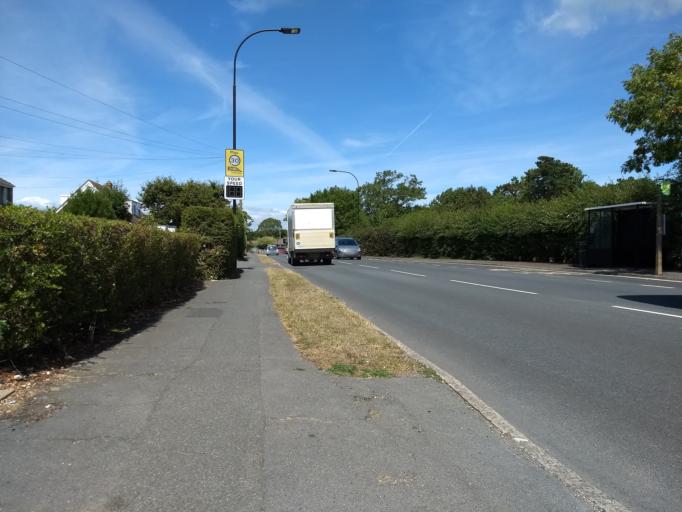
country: GB
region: England
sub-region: Isle of Wight
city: Northwood
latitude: 50.7417
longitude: -1.3095
